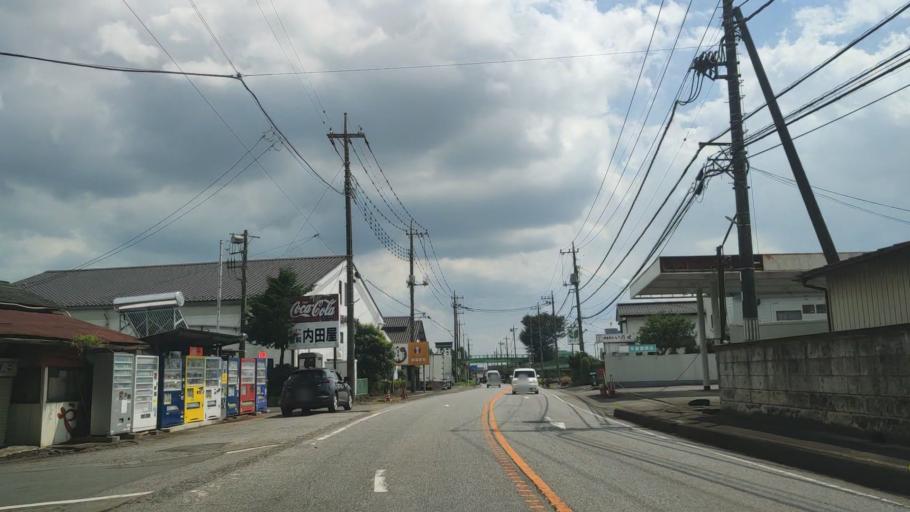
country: JP
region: Tochigi
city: Utsunomiya-shi
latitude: 36.6561
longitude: 139.8409
